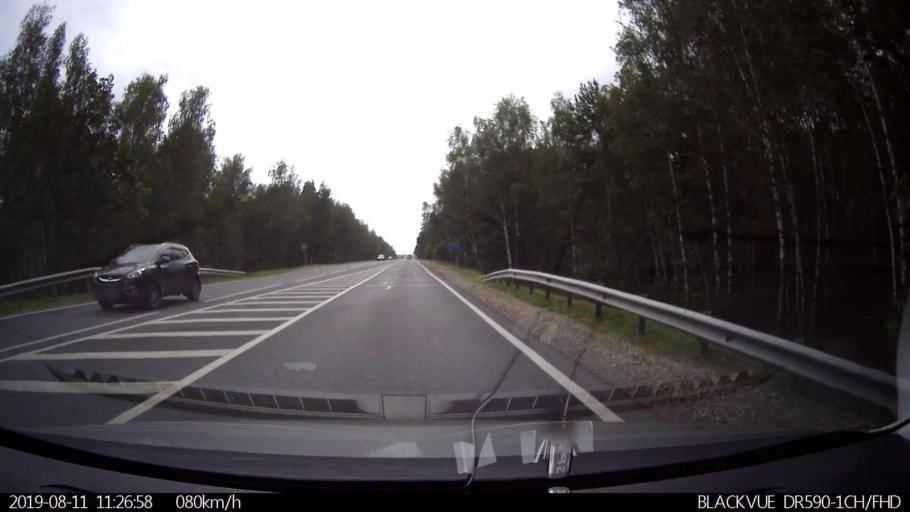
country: RU
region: Ulyanovsk
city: Krasnyy Gulyay
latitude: 54.0991
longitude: 48.2333
